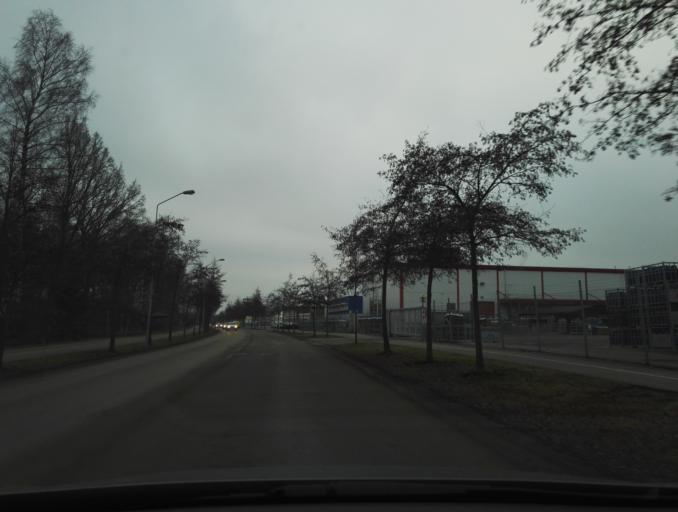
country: SE
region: Kronoberg
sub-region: Vaxjo Kommun
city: Vaexjoe
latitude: 56.8874
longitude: 14.7825
